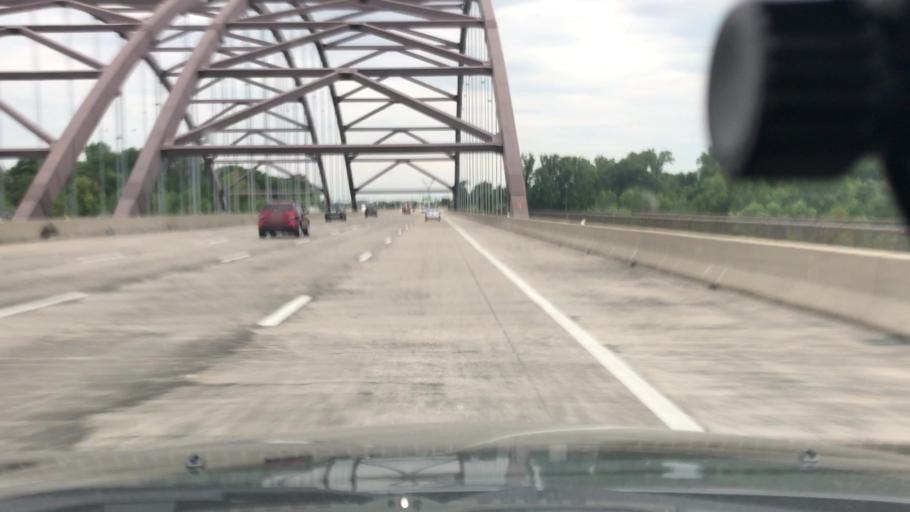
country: US
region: Missouri
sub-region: Saint Charles County
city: Saint Charles
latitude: 38.7363
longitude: -90.5216
